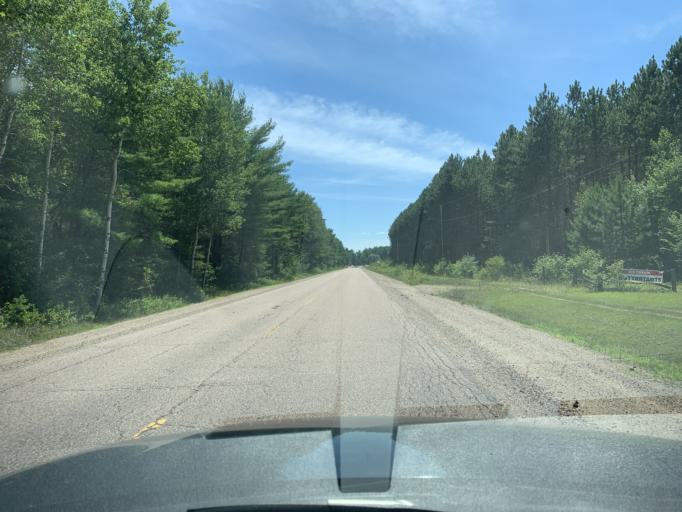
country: CA
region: Ontario
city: Petawawa
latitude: 45.6500
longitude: -77.5781
